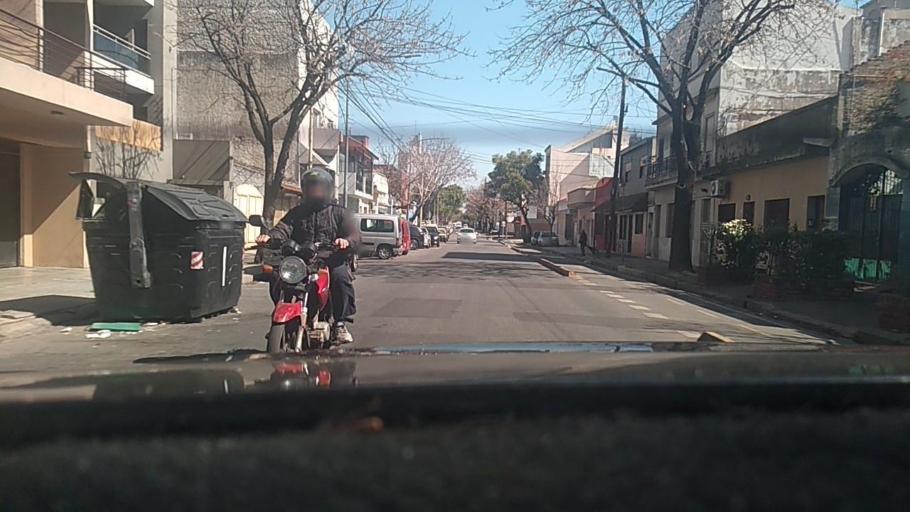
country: AR
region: Buenos Aires F.D.
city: Villa Santa Rita
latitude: -34.6136
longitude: -58.5054
